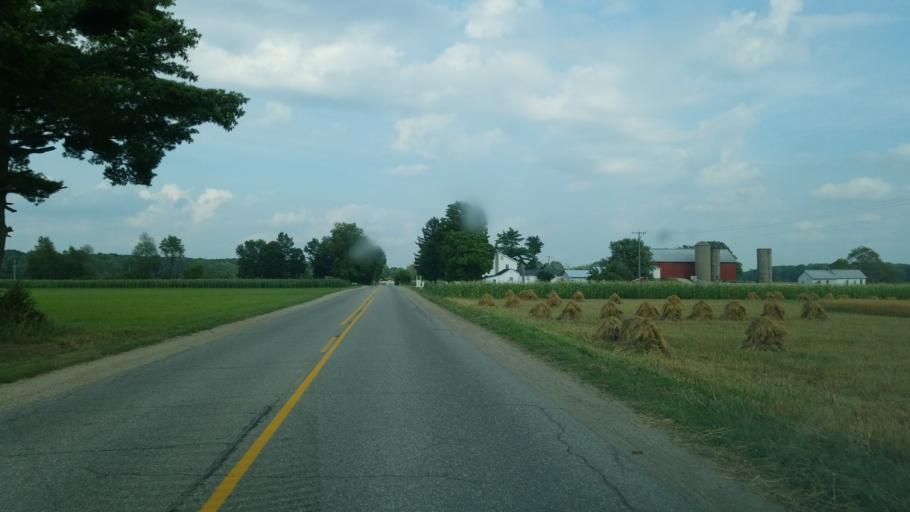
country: US
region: Michigan
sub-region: Mecosta County
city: Canadian Lakes
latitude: 43.5424
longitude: -85.3410
